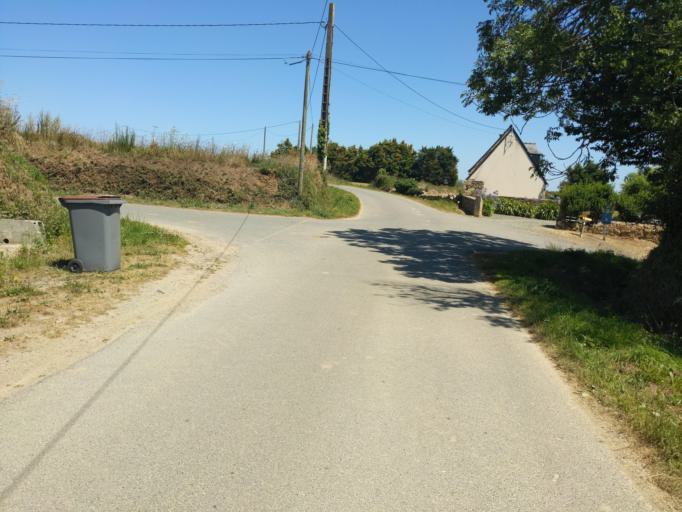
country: FR
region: Brittany
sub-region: Departement des Cotes-d'Armor
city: Plouguiel
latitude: 48.8075
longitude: -3.2189
